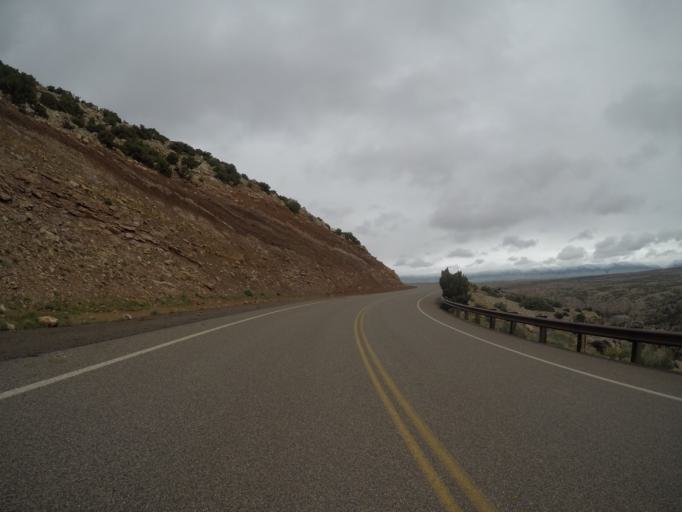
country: US
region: Wyoming
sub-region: Big Horn County
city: Lovell
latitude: 45.0419
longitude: -108.2530
